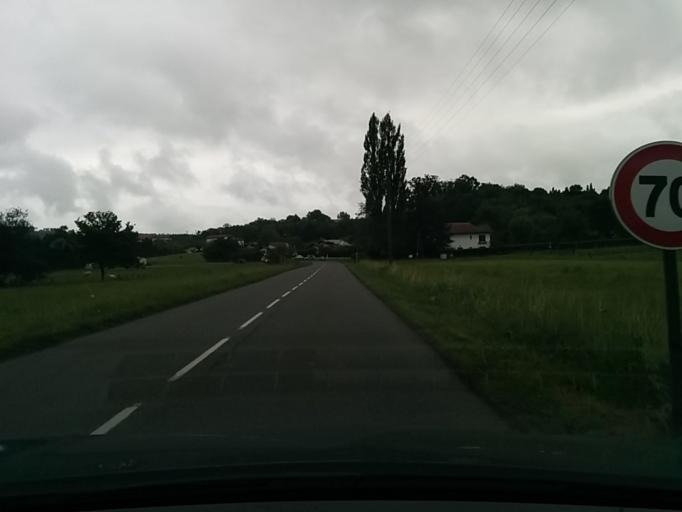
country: FR
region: Aquitaine
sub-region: Departement des Pyrenees-Atlantiques
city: Saint-Pee-sur-Nivelle
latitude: 43.3472
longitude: -1.5523
